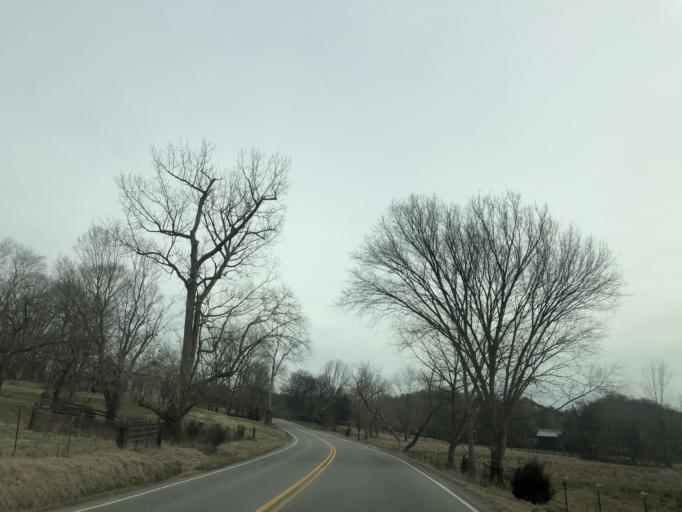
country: US
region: Tennessee
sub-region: Sumner County
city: White House
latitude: 36.5173
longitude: -86.6198
